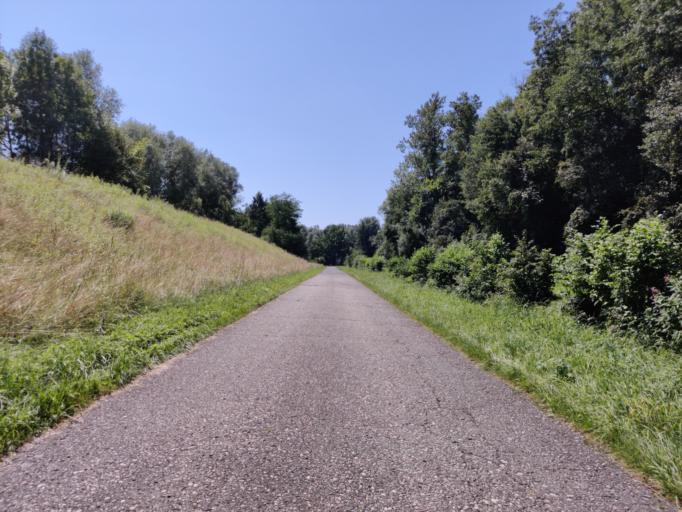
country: AT
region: Styria
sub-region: Politischer Bezirk Leibnitz
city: Gabersdorf
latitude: 46.7873
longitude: 15.5840
